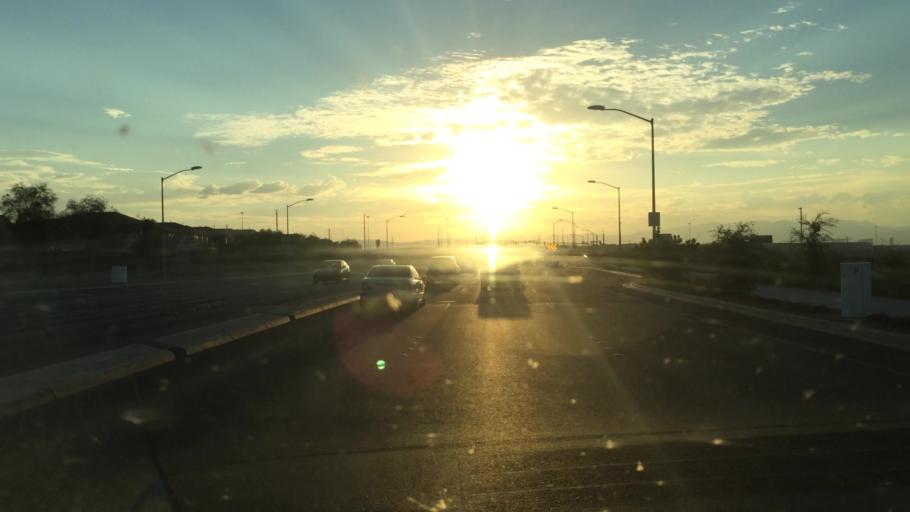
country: US
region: Nevada
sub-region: Clark County
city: Whitney
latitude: 36.0711
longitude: -115.0291
